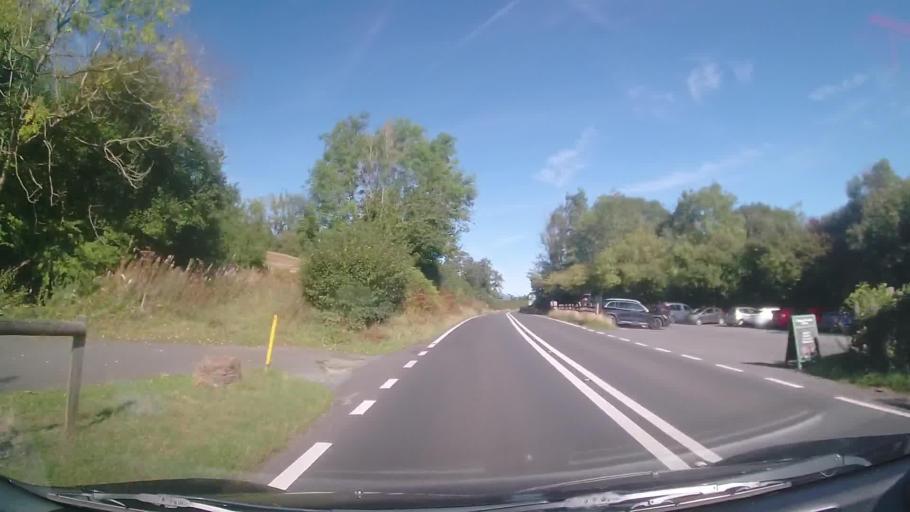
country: GB
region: Wales
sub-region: Sir Powys
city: Hay
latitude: 51.9591
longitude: -3.2035
